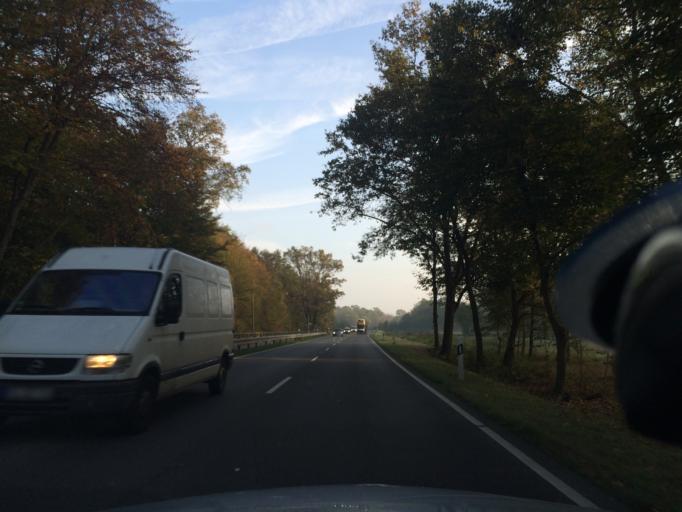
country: DE
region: Hesse
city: Morfelden-Walldorf
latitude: 49.9618
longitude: 8.5465
